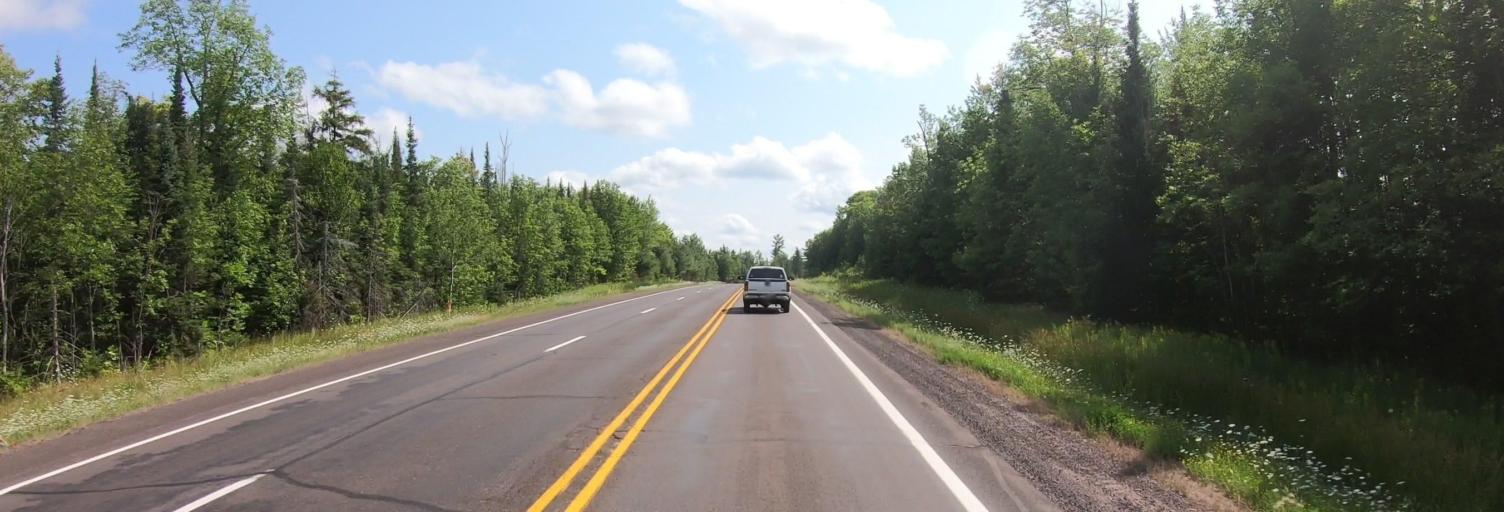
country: US
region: Michigan
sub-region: Ontonagon County
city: Ontonagon
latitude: 46.8117
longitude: -88.9962
